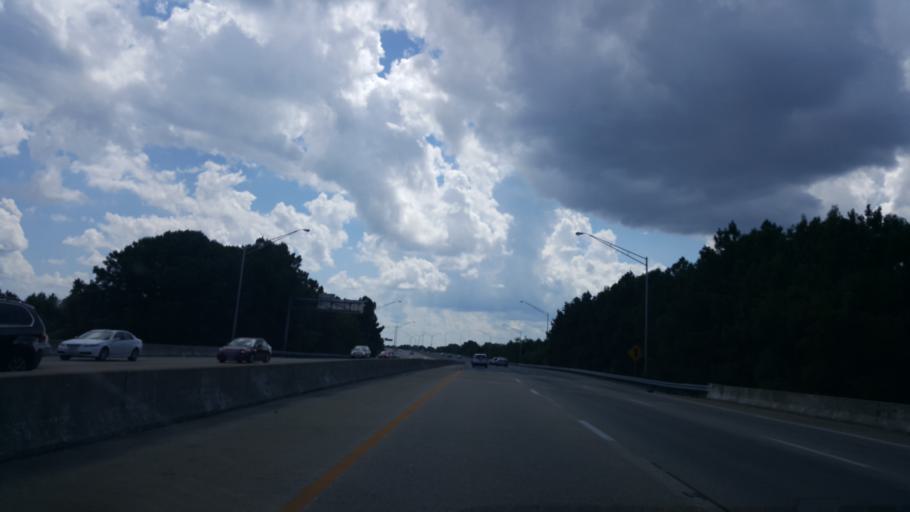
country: US
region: Virginia
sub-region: City of Newport News
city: Newport News
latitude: 37.0041
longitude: -76.4031
